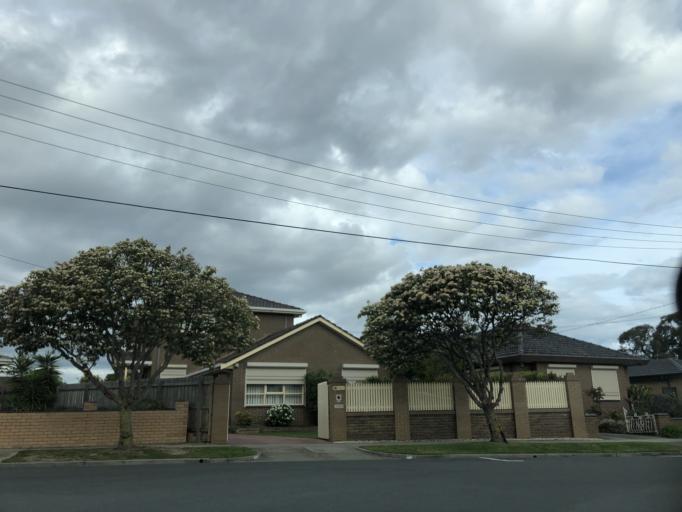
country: AU
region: Victoria
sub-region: Monash
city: Oakleigh South
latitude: -37.9217
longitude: 145.0938
